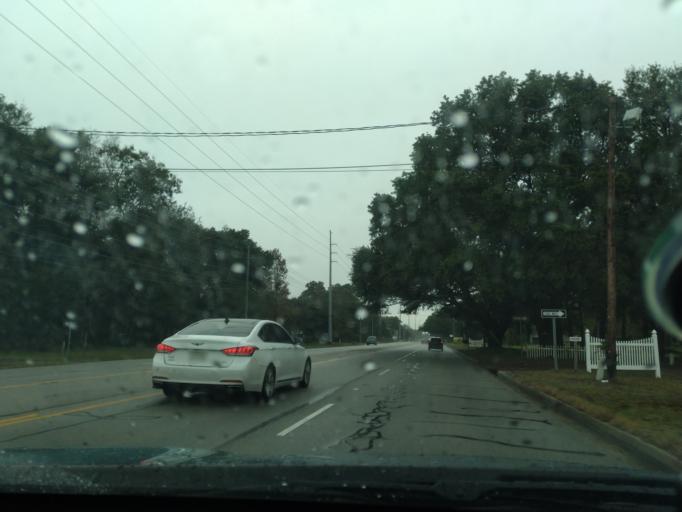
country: US
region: South Carolina
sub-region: Charleston County
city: Folly Beach
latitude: 32.7113
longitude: -79.9643
